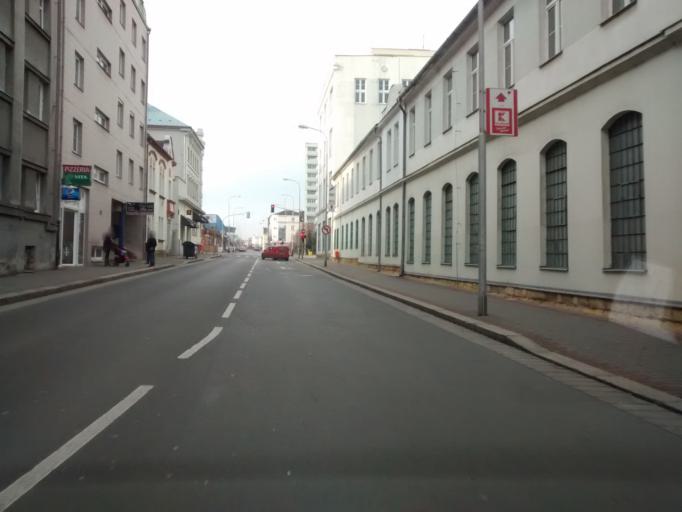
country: CZ
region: Central Bohemia
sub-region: Okres Mlada Boleslav
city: Mlada Boleslav
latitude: 50.4178
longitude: 14.9140
